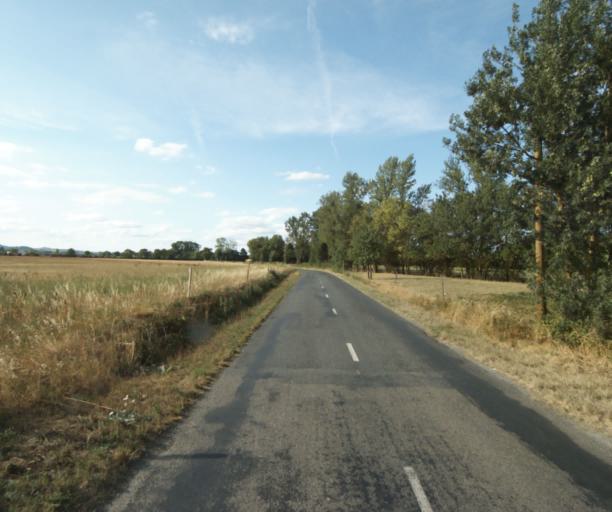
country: FR
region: Midi-Pyrenees
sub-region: Departement de la Haute-Garonne
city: Revel
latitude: 43.4773
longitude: 1.9908
